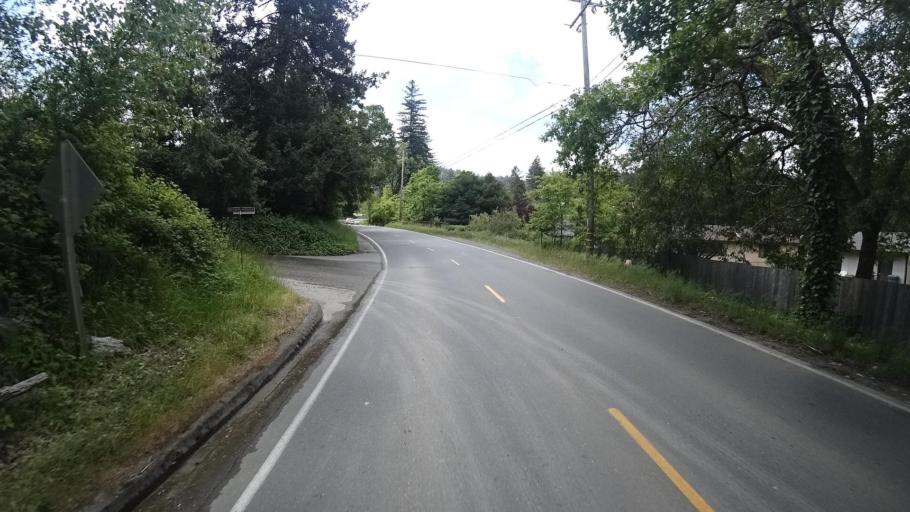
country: US
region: California
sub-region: Humboldt County
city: Redway
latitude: 40.1228
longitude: -123.8308
